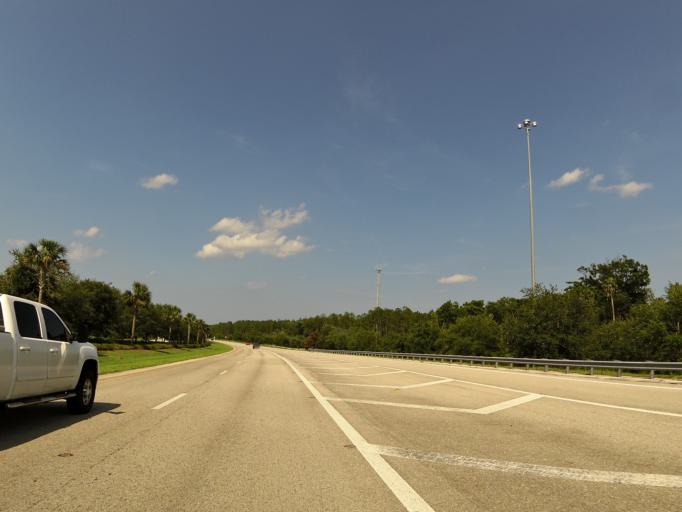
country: US
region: Florida
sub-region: Saint Johns County
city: Palm Valley
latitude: 30.1149
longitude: -81.4140
